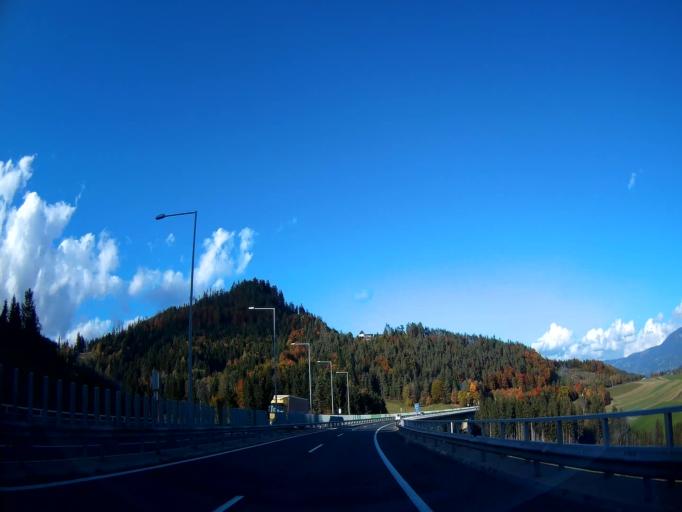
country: AT
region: Carinthia
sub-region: Politischer Bezirk Volkermarkt
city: Griffen
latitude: 46.7100
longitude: 14.7786
